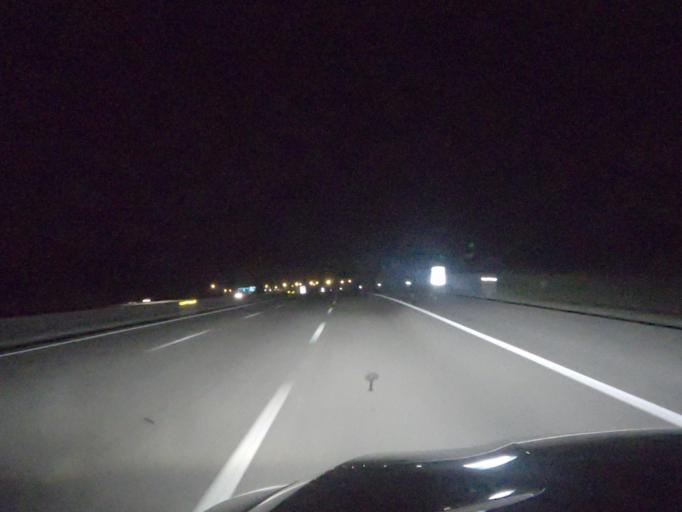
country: PT
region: Santarem
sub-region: Alcanena
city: Alcanena
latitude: 39.4678
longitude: -8.6288
